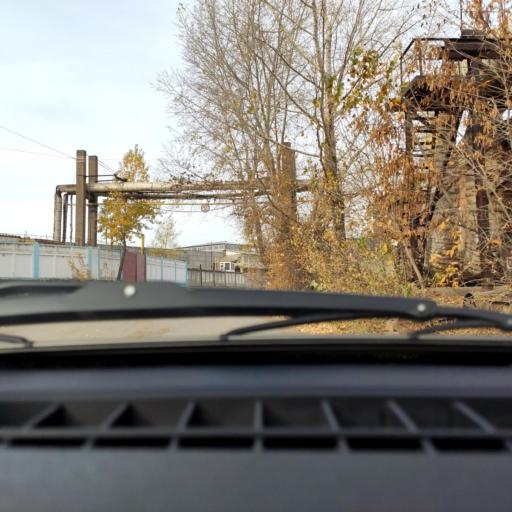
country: RU
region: Bashkortostan
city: Ufa
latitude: 54.8334
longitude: 56.1174
